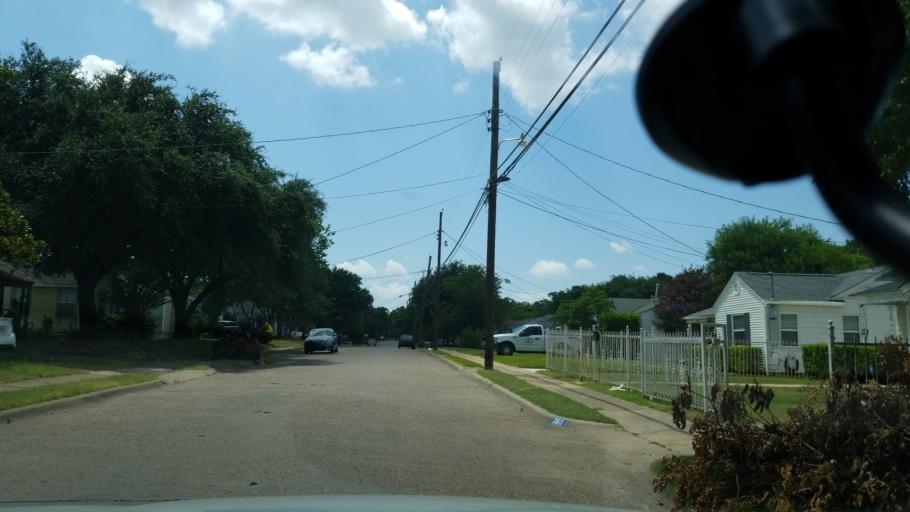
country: US
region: Texas
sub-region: Dallas County
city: Cockrell Hill
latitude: 32.7264
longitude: -96.8796
